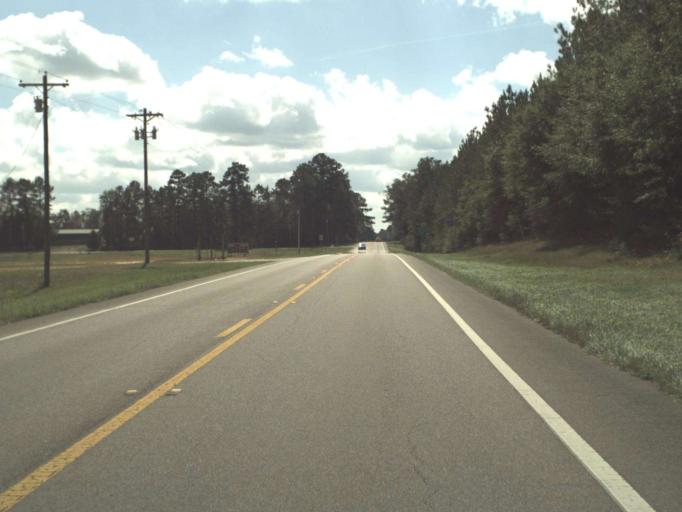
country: US
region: Florida
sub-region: Walton County
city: DeFuniak Springs
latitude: 30.6629
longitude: -85.9366
